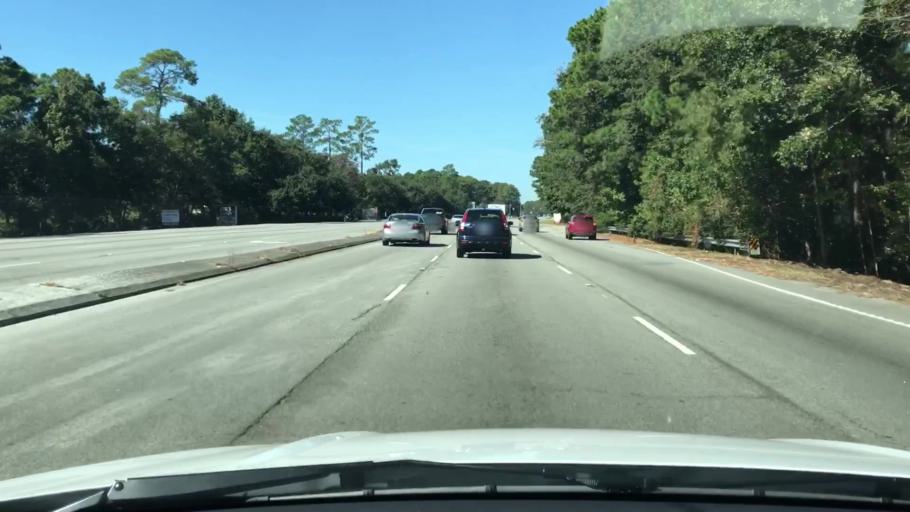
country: US
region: South Carolina
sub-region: Beaufort County
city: Bluffton
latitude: 32.2557
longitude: -80.8486
